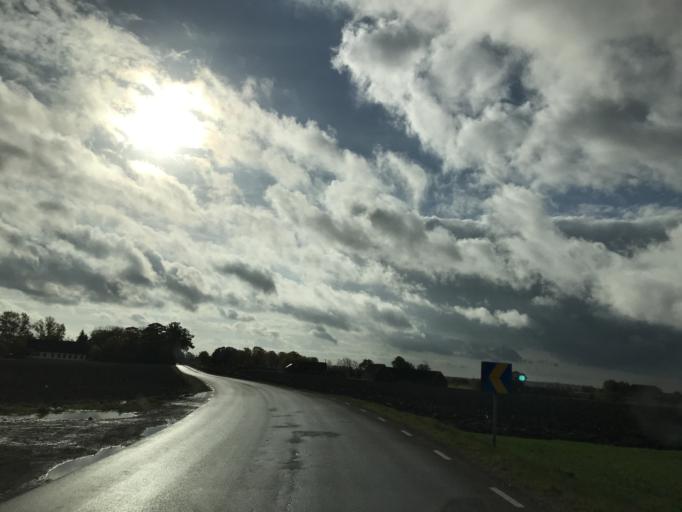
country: SE
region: Skane
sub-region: Svalovs Kommun
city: Teckomatorp
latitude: 55.8750
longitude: 13.1175
